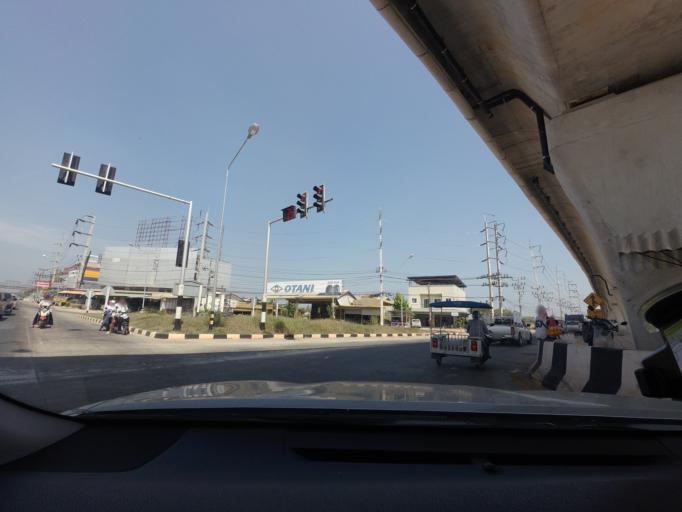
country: TH
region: Surat Thani
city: Surat Thani
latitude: 9.1515
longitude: 99.3688
